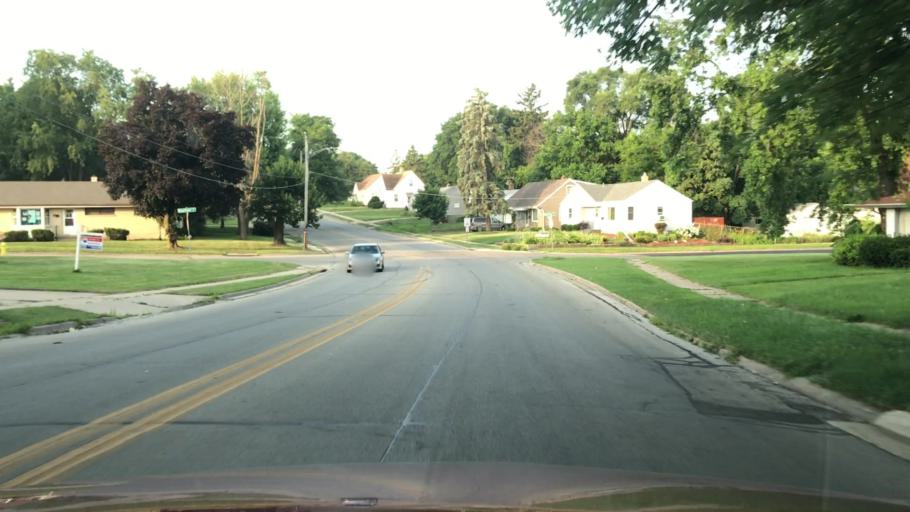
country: US
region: Illinois
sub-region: Winnebago County
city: Rockford
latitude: 42.2604
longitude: -89.0426
